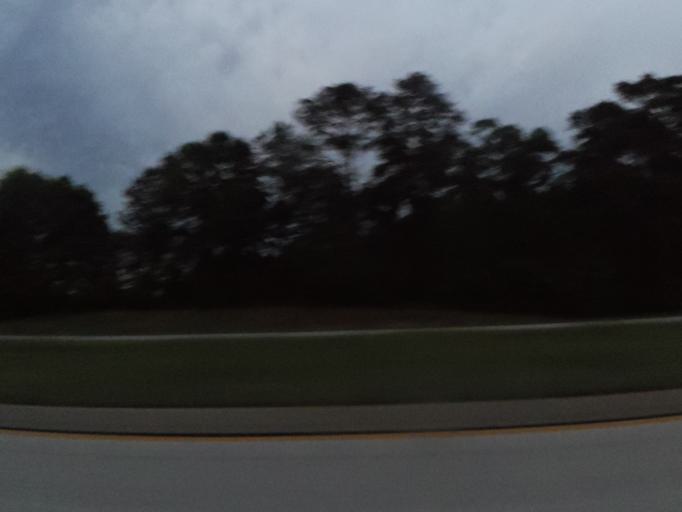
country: US
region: Georgia
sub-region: McDuffie County
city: Thomson
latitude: 33.5132
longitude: -82.4669
